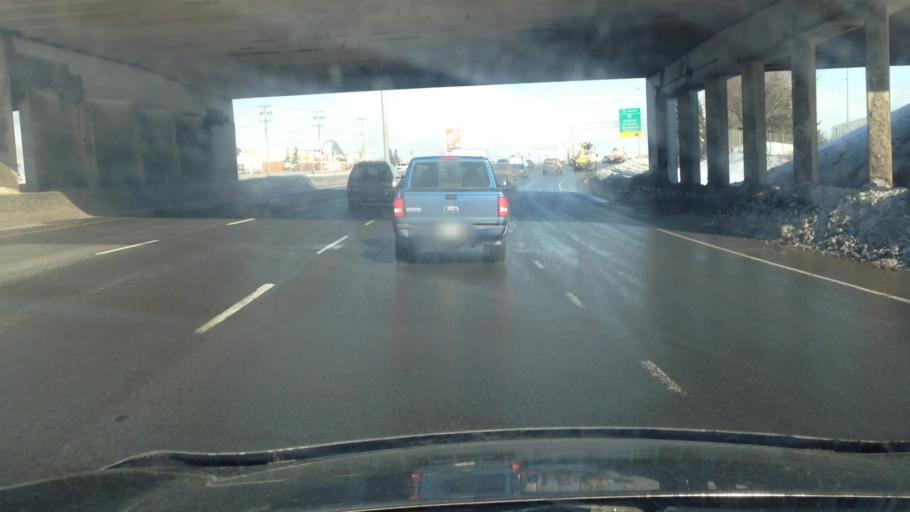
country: CA
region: Quebec
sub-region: Laurentides
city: Boisbriand
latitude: 45.6213
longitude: -73.8488
